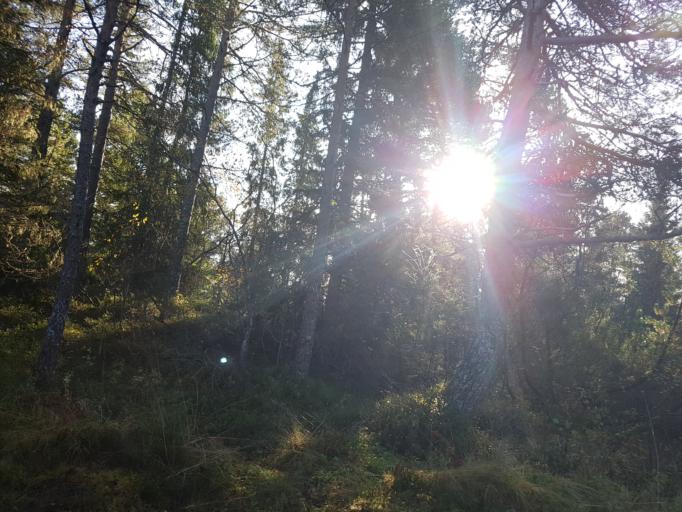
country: NO
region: Sor-Trondelag
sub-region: Trondheim
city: Trondheim
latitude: 63.4084
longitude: 10.3311
